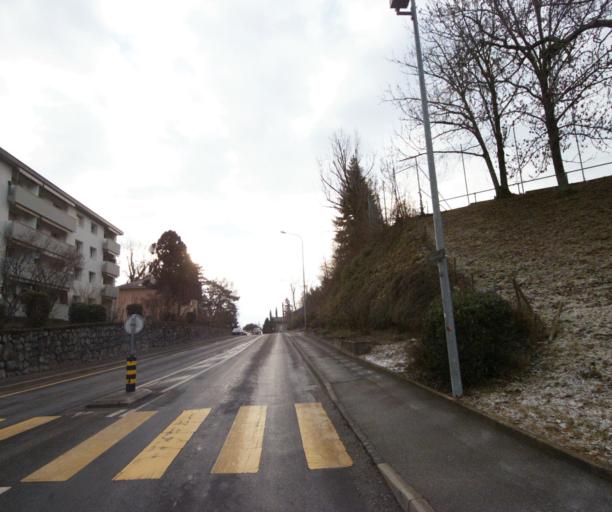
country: CH
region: Vaud
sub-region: Riviera-Pays-d'Enhaut District
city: La Tour-de-Peilz
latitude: 46.4537
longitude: 6.8680
